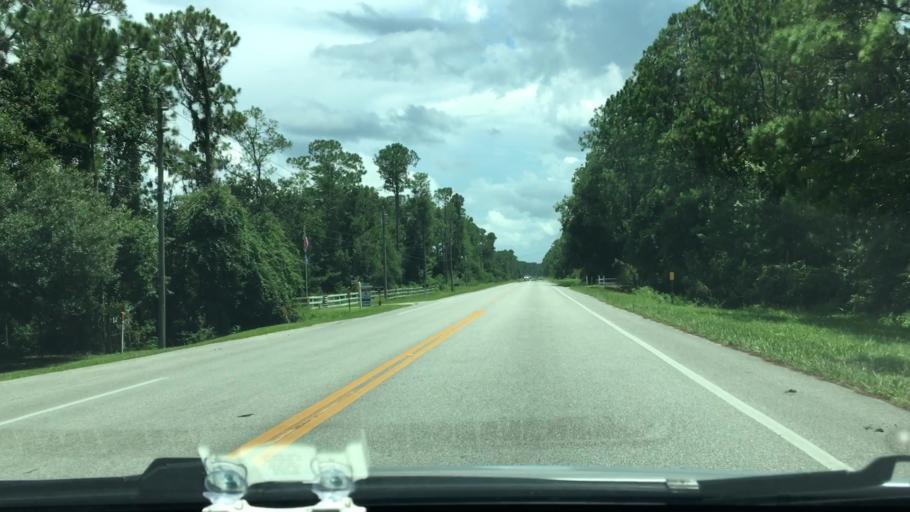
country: US
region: Florida
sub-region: Volusia County
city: Samsula-Spruce Creek
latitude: 29.0406
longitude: -81.0672
